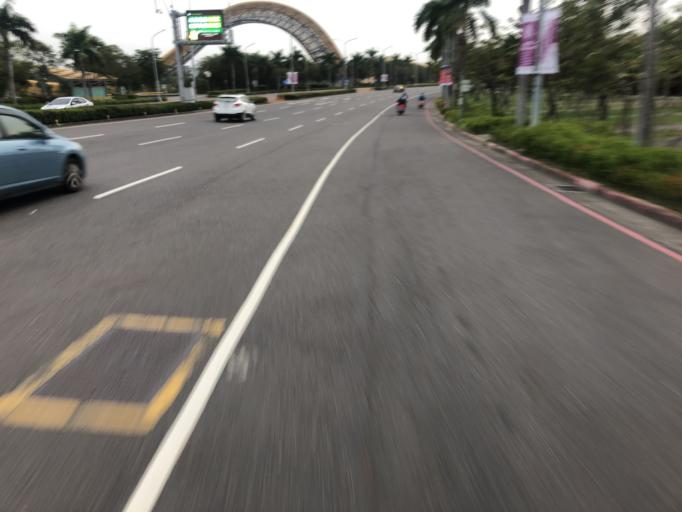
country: TW
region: Taiwan
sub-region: Tainan
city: Tainan
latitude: 23.0895
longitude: 120.2826
